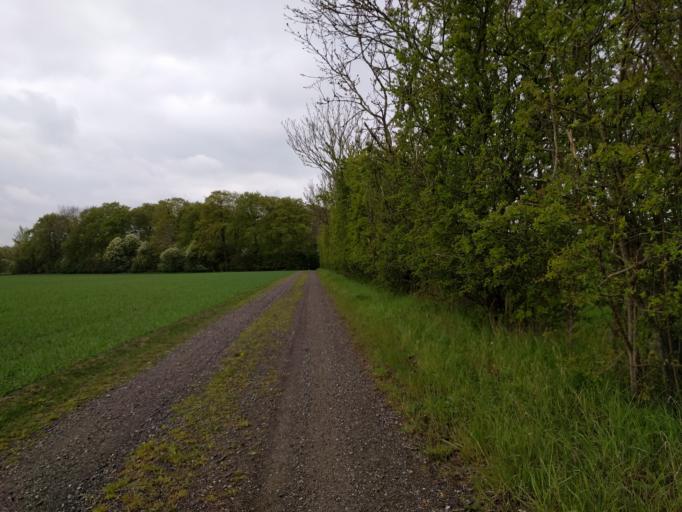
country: DK
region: South Denmark
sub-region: Kerteminde Kommune
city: Langeskov
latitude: 55.3974
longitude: 10.5765
